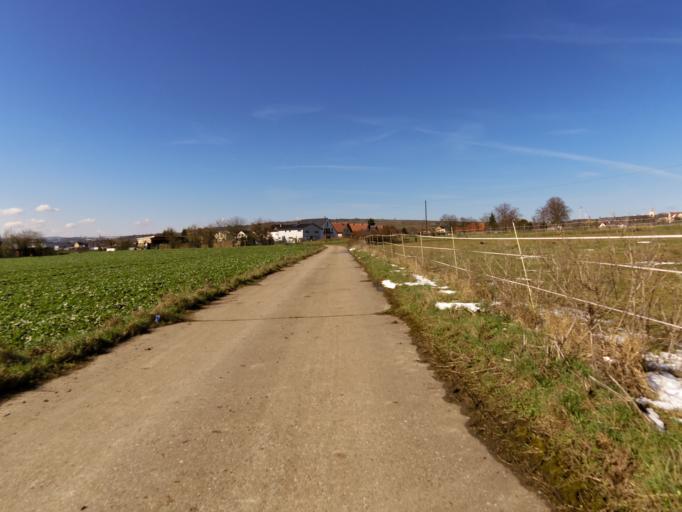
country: DE
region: Rheinland-Pfalz
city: Bockenheim
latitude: 49.6109
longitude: 8.1928
